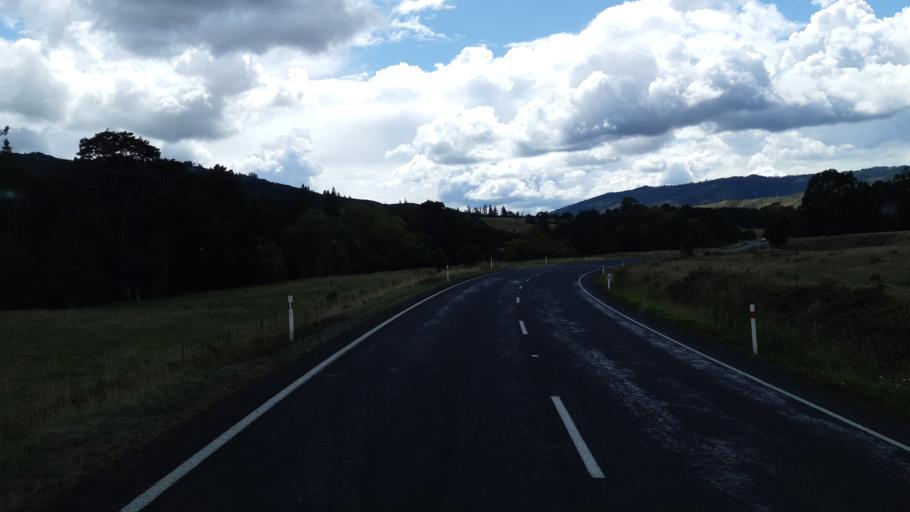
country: NZ
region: Tasman
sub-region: Tasman District
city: Wakefield
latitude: -41.5629
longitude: 172.7791
